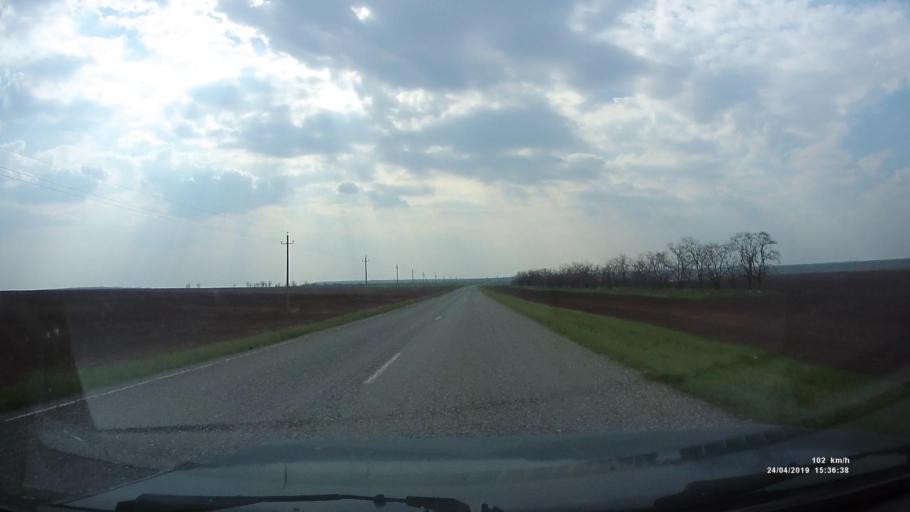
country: RU
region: Kalmykiya
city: Yashalta
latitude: 46.5990
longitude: 42.8668
